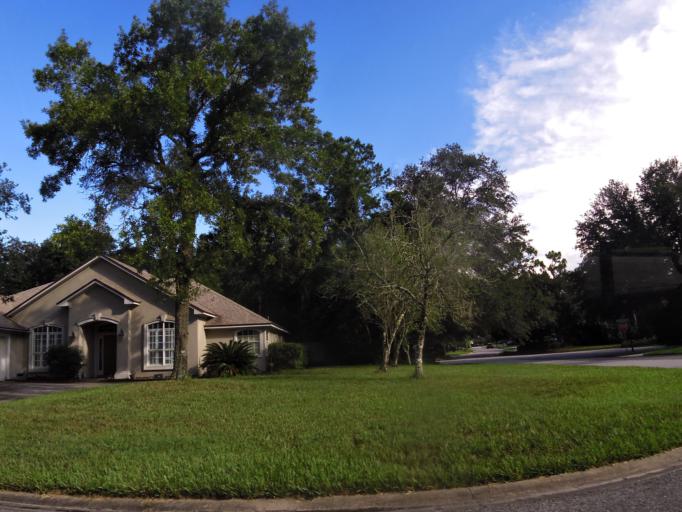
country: US
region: Florida
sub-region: Saint Johns County
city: Fruit Cove
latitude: 30.2124
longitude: -81.5339
